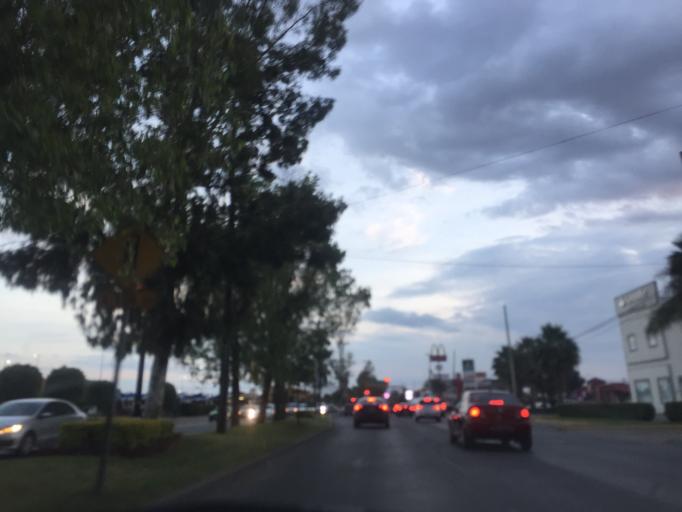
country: MX
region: Guanajuato
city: Leon
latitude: 21.1628
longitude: -101.6928
